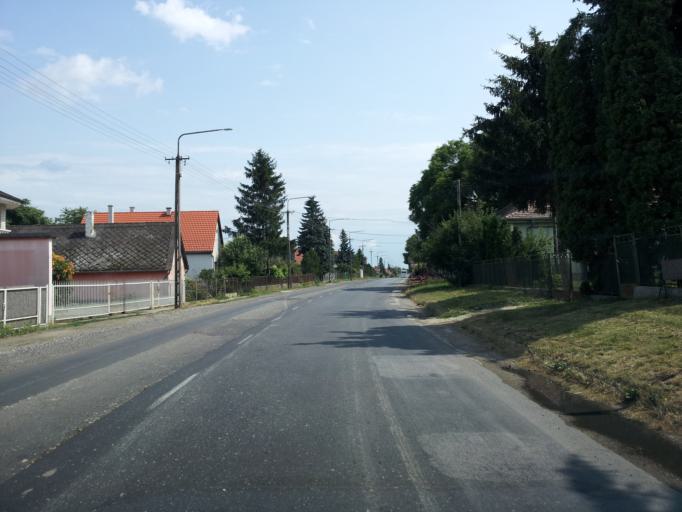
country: HU
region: Fejer
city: Enying
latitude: 46.9506
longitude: 18.2282
